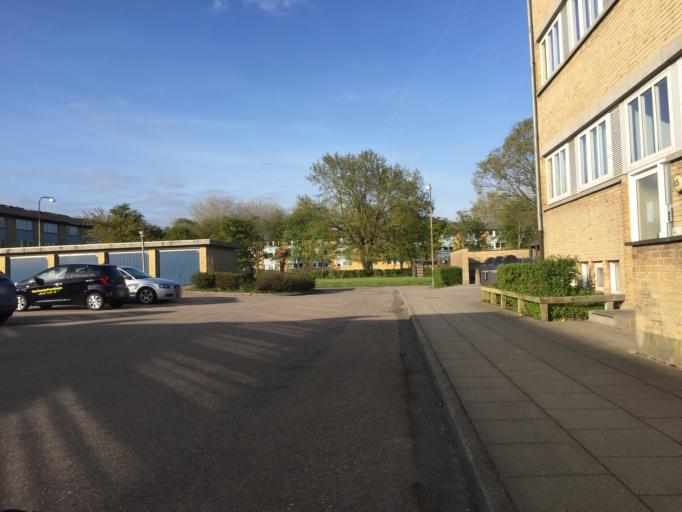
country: DK
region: South Denmark
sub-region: Odense Kommune
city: Neder Holluf
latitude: 55.3765
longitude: 10.4223
